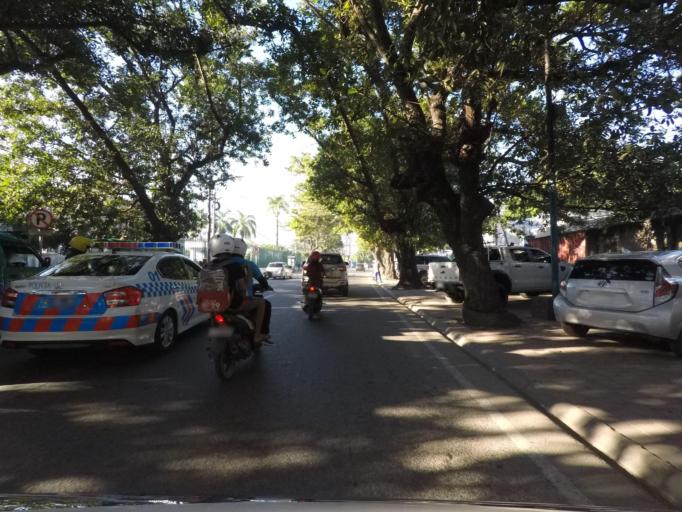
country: TL
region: Dili
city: Dili
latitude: -8.5540
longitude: 125.5796
